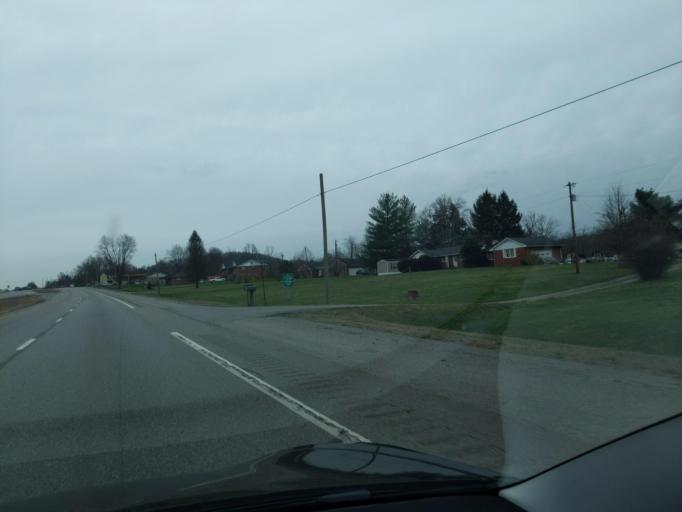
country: US
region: Kentucky
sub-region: Knox County
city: Barbourville
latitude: 36.8563
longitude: -83.7926
